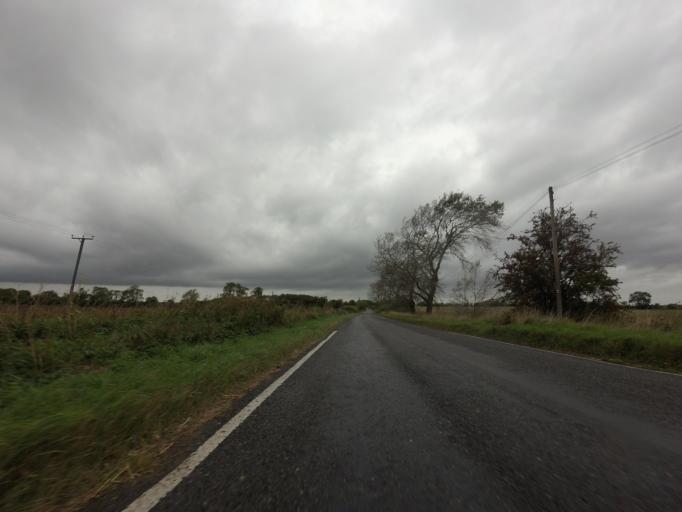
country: GB
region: England
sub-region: Cambridgeshire
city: Wimpole
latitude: 52.1732
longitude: -0.0239
